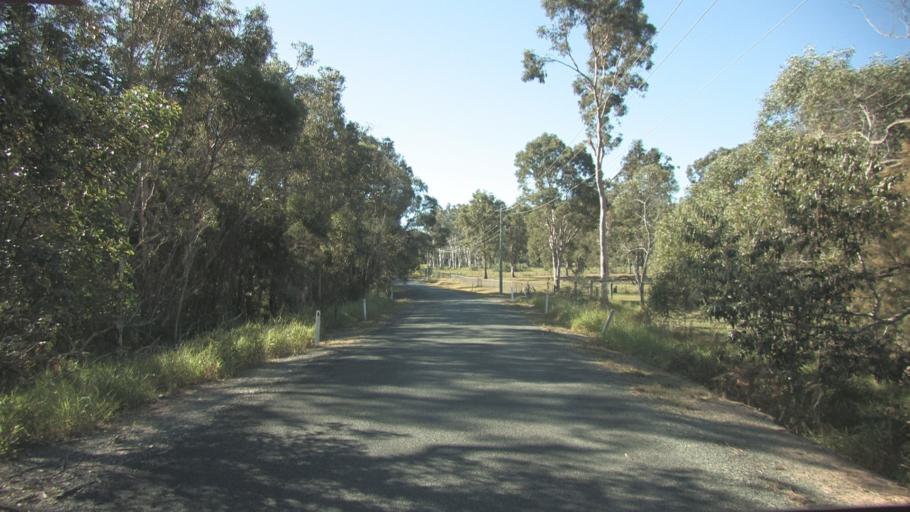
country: AU
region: Queensland
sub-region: Logan
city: Logan Reserve
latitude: -27.7317
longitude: 153.0826
